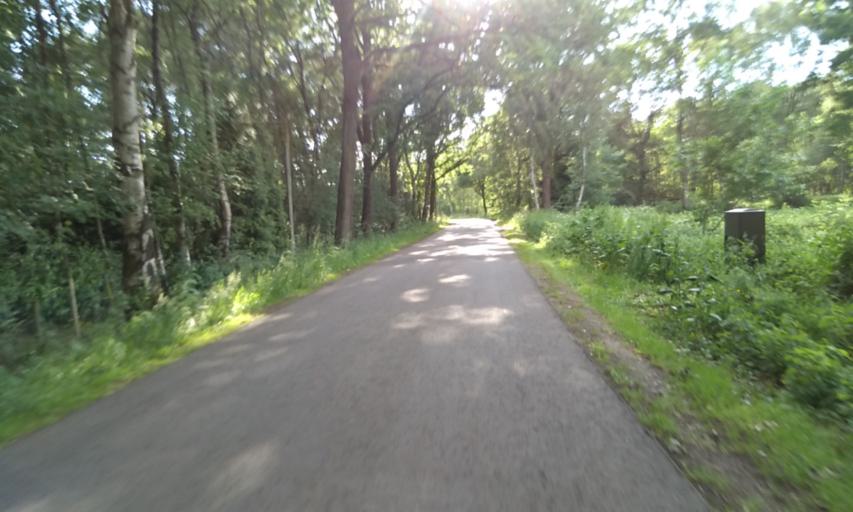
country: DE
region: Lower Saxony
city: Ahlerstedt
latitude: 53.3609
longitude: 9.4604
